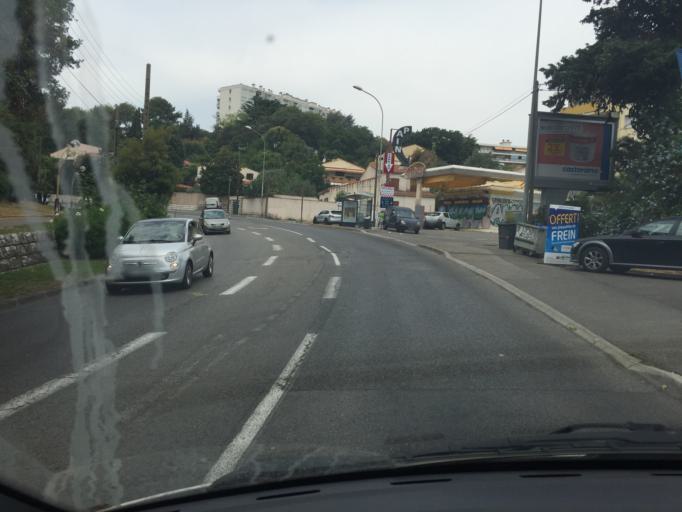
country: FR
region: Provence-Alpes-Cote d'Azur
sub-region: Departement des Alpes-Maritimes
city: Biot
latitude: 43.5941
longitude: 7.0984
